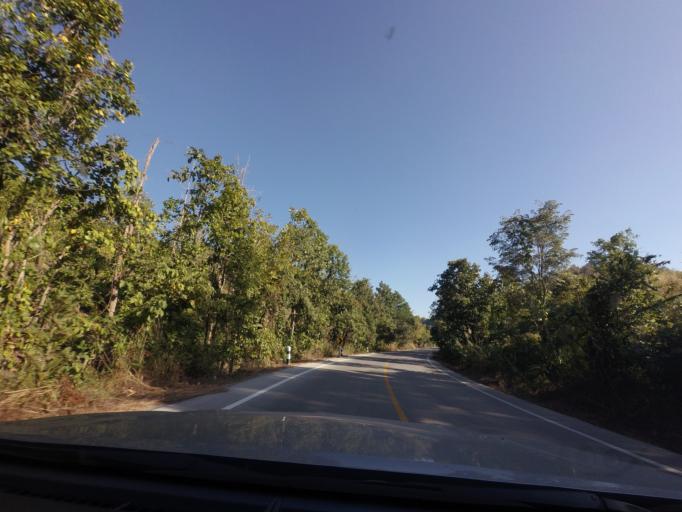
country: TH
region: Lampang
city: Chae Hom
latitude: 18.5622
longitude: 99.6243
